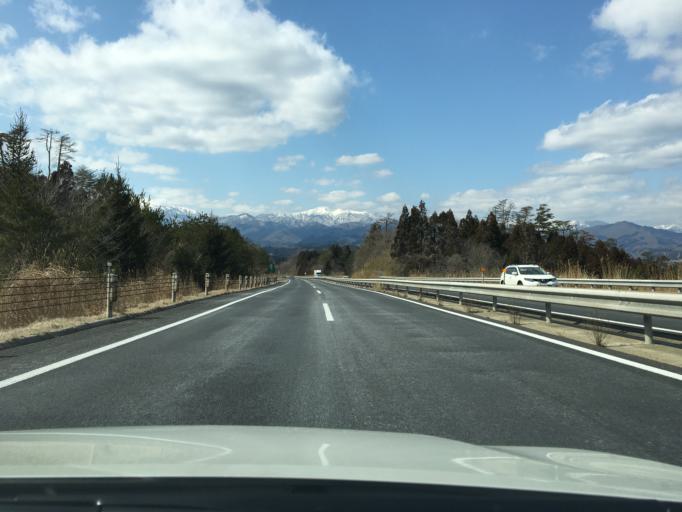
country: JP
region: Miyagi
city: Okawara
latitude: 38.1640
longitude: 140.6596
